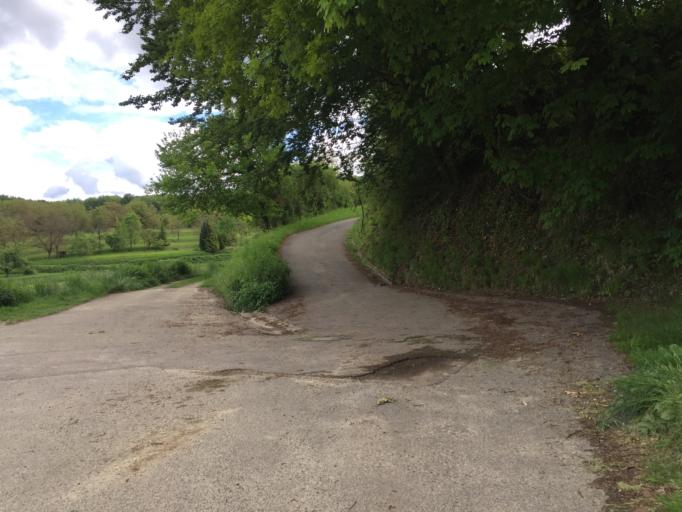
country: DE
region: Baden-Wuerttemberg
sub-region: Freiburg Region
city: Malterdingen
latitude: 48.1577
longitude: 7.8126
